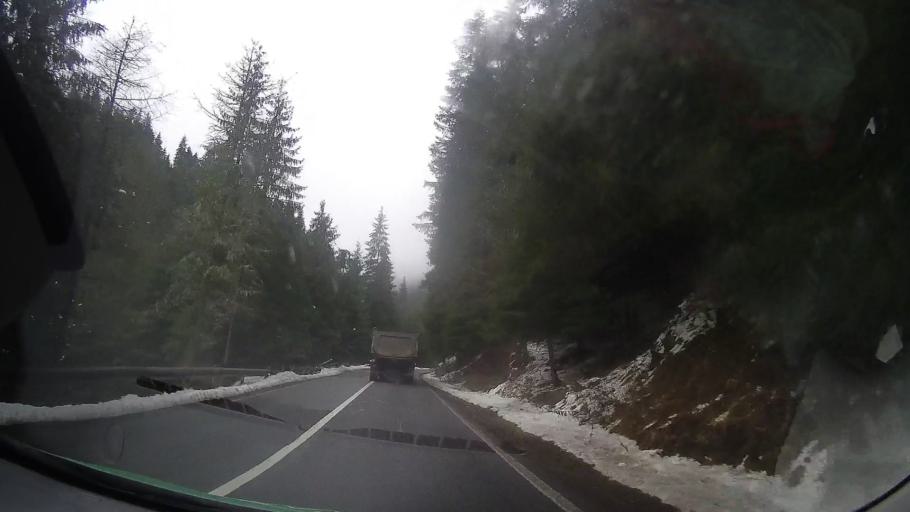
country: RO
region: Neamt
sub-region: Comuna Bicaz Chei
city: Bicaz Chei
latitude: 46.7812
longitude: 25.7502
